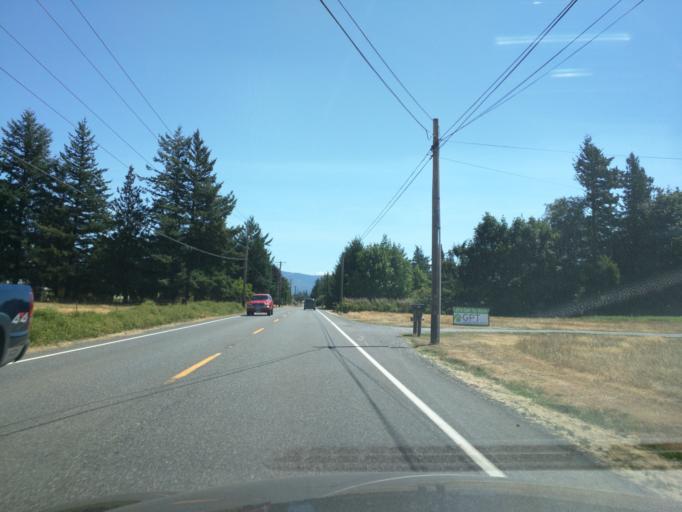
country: US
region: Washington
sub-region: Whatcom County
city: Lynden
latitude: 48.8917
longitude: -122.4551
